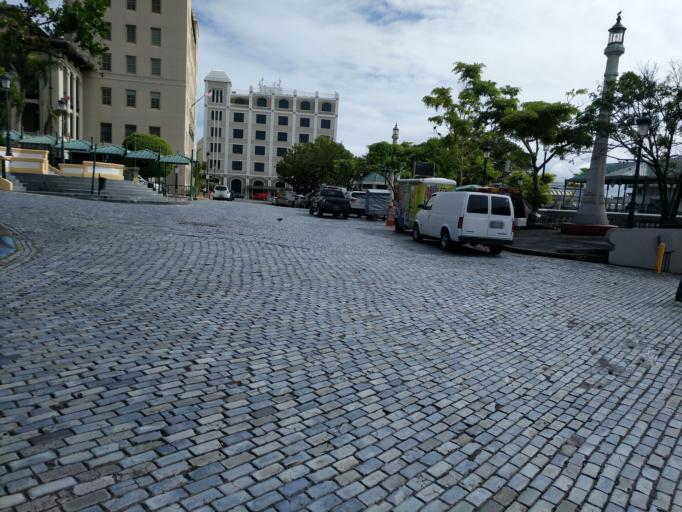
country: PR
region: San Juan
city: San Juan
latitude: 18.4634
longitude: -66.1154
